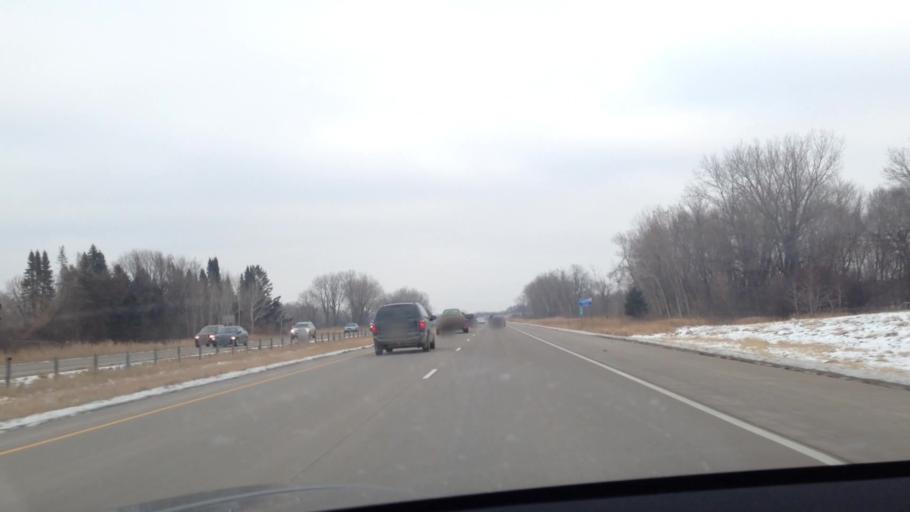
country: US
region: Minnesota
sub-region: Anoka County
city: Lino Lakes
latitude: 45.1888
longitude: -93.0862
